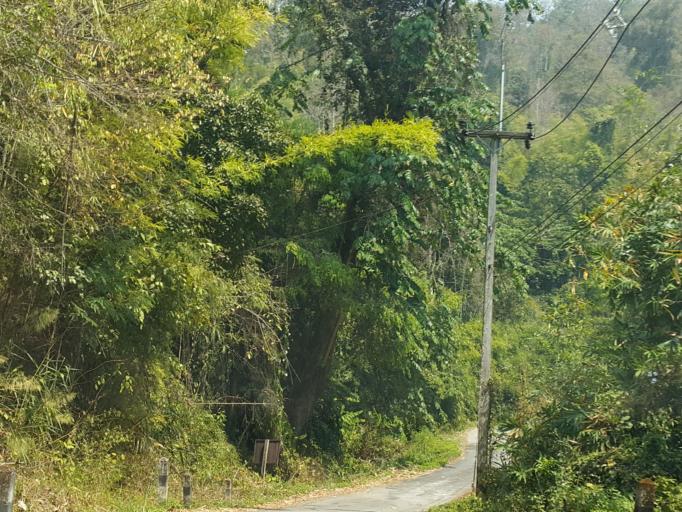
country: TH
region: Lampang
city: Mueang Pan
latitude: 18.8188
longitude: 99.4411
